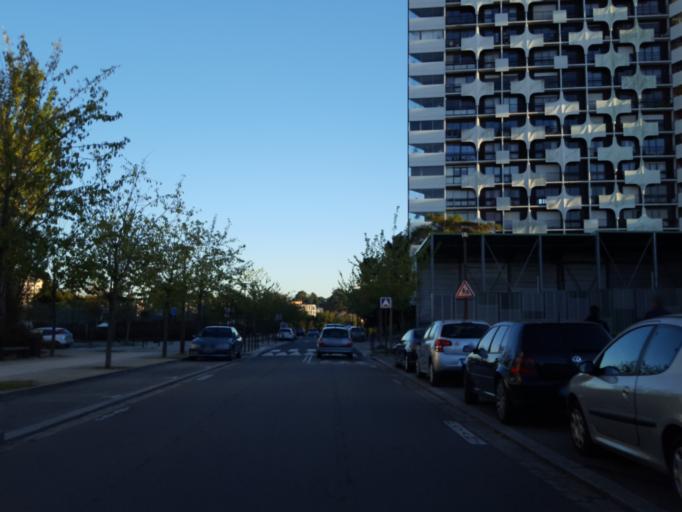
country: FR
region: Pays de la Loire
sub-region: Departement de la Loire-Atlantique
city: Nantes
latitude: 47.2058
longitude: -1.5325
